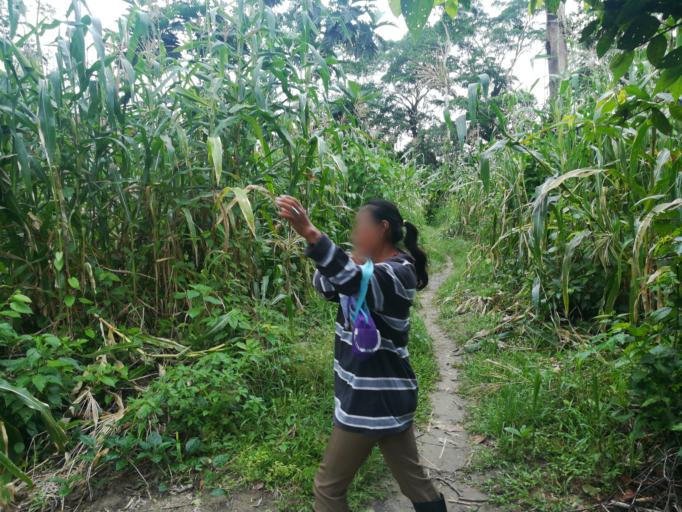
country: EC
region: Orellana
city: Boca Suno
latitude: -0.7517
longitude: -77.1534
